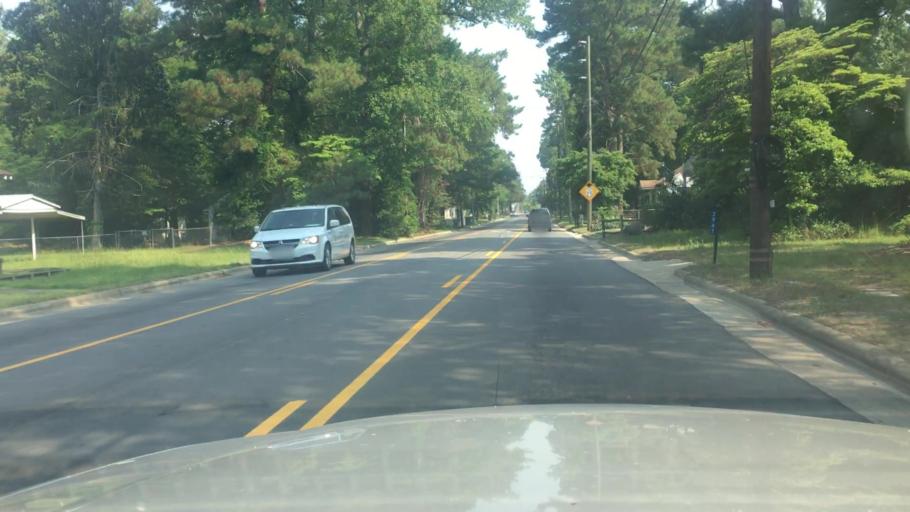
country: US
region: North Carolina
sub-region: Cumberland County
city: Hope Mills
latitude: 34.9668
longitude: -78.9443
